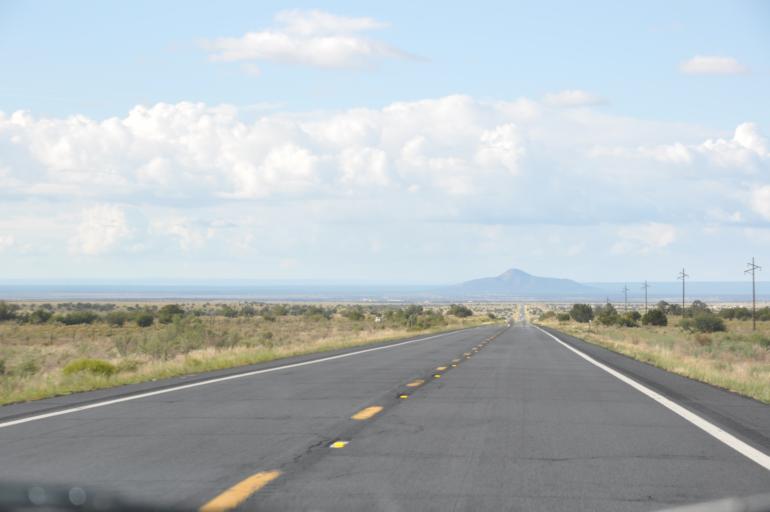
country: US
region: Arizona
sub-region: Coconino County
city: Williams
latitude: 35.5448
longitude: -112.1619
